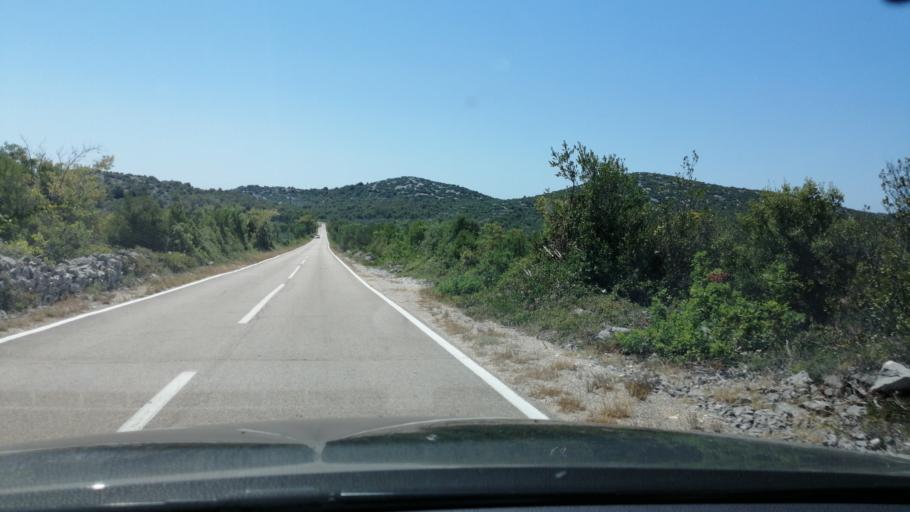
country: HR
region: Sibensko-Kniniska
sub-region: Grad Sibenik
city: Pirovac
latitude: 43.8515
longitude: 15.6877
